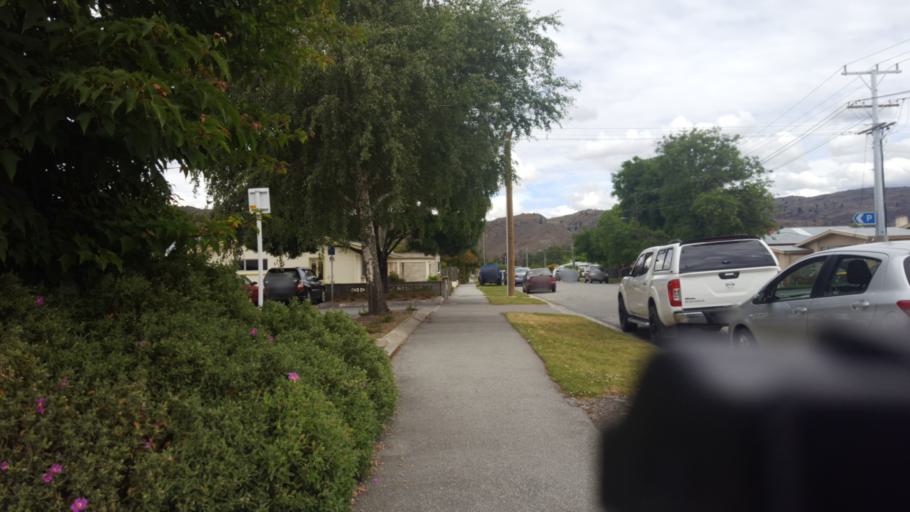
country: NZ
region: Otago
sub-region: Queenstown-Lakes District
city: Wanaka
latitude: -45.2526
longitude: 169.3876
